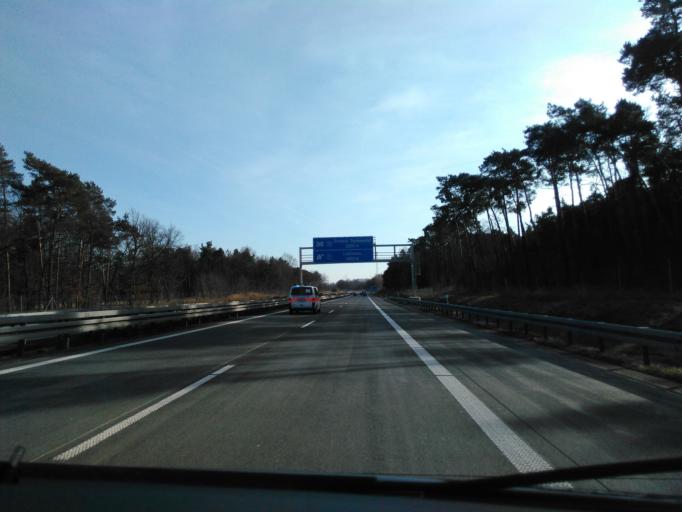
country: DE
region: Brandenburg
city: Lubbenau
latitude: 51.8627
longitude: 13.9017
